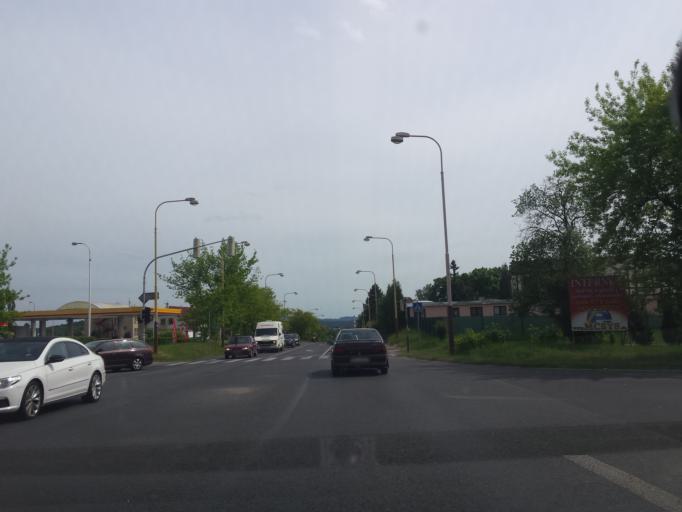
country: CZ
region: Liberecky
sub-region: Okres Ceska Lipa
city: Ceska Lipa
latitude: 50.6935
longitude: 14.5414
